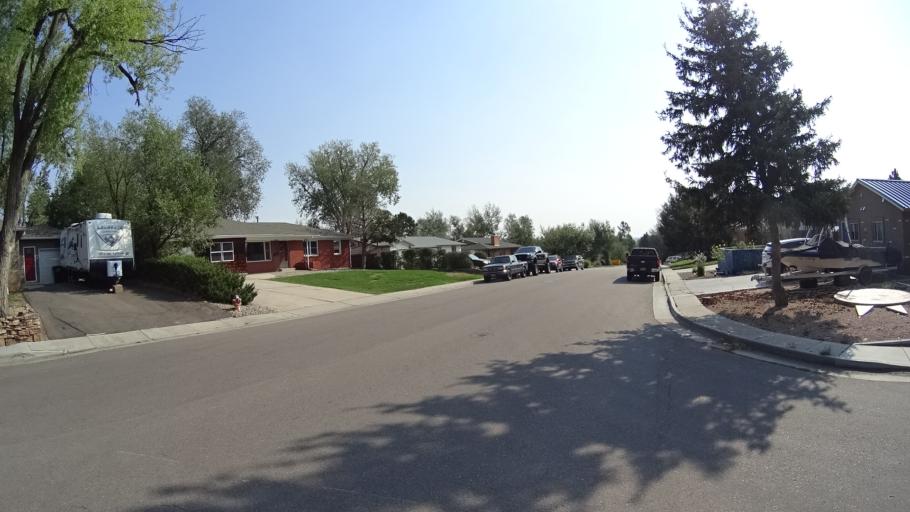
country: US
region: Colorado
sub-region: El Paso County
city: Colorado Springs
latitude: 38.8090
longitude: -104.8394
